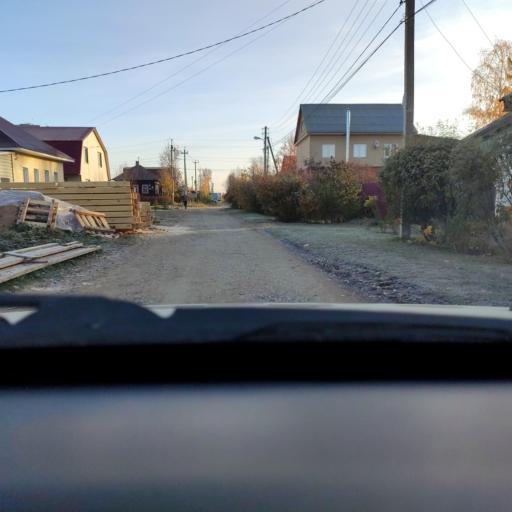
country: RU
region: Perm
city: Perm
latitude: 58.0264
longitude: 56.3249
